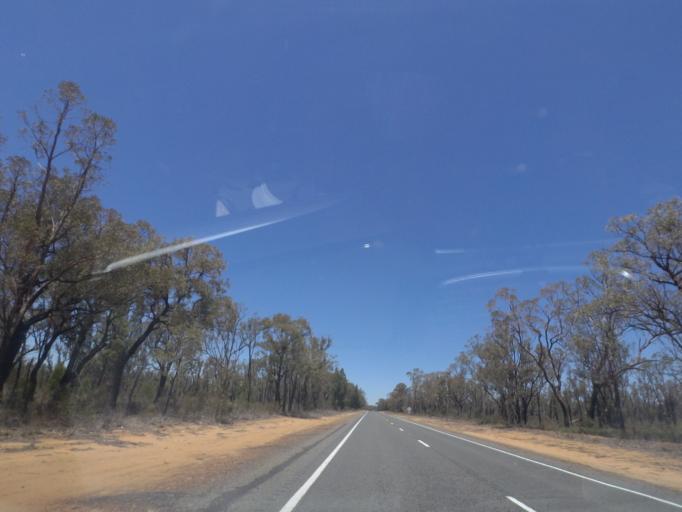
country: AU
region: New South Wales
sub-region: Narrabri
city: Narrabri
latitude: -30.7123
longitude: 149.5294
